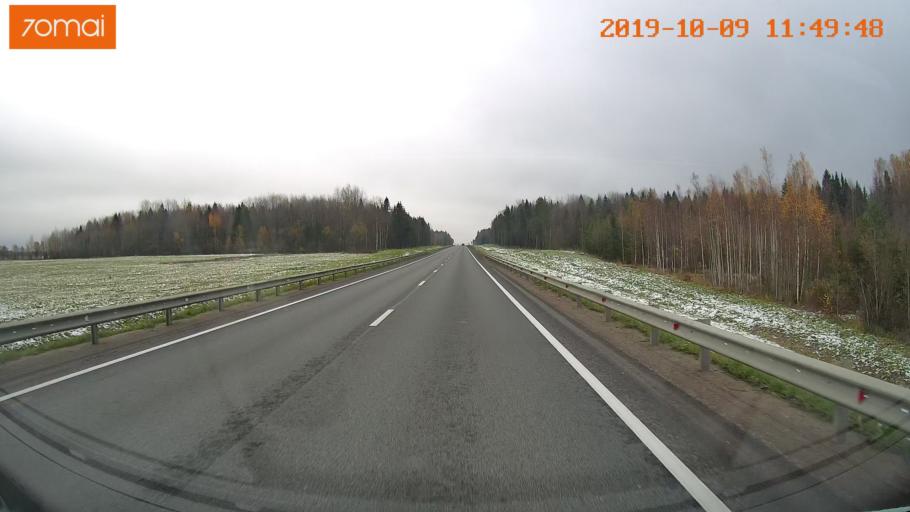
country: RU
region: Vologda
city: Gryazovets
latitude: 58.8138
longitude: 40.2360
